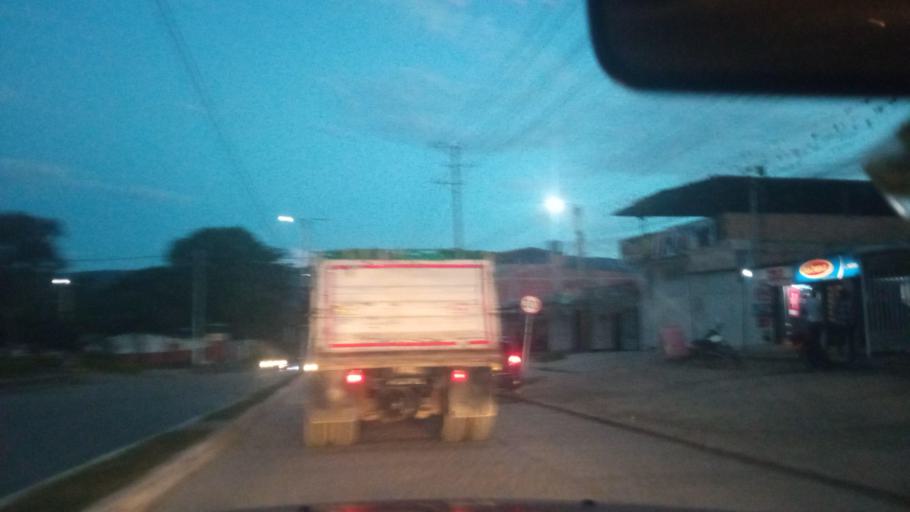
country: CO
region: Huila
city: Pitalito
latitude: 1.8605
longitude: -76.0494
